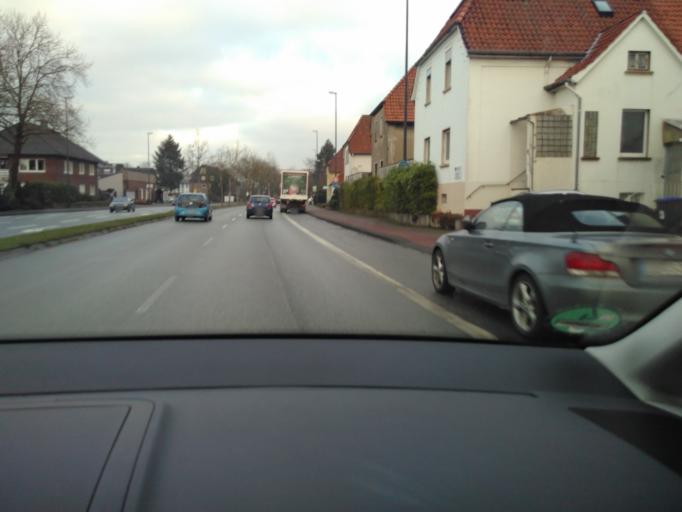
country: DE
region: North Rhine-Westphalia
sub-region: Regierungsbezirk Detmold
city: Guetersloh
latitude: 51.9035
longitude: 8.3589
